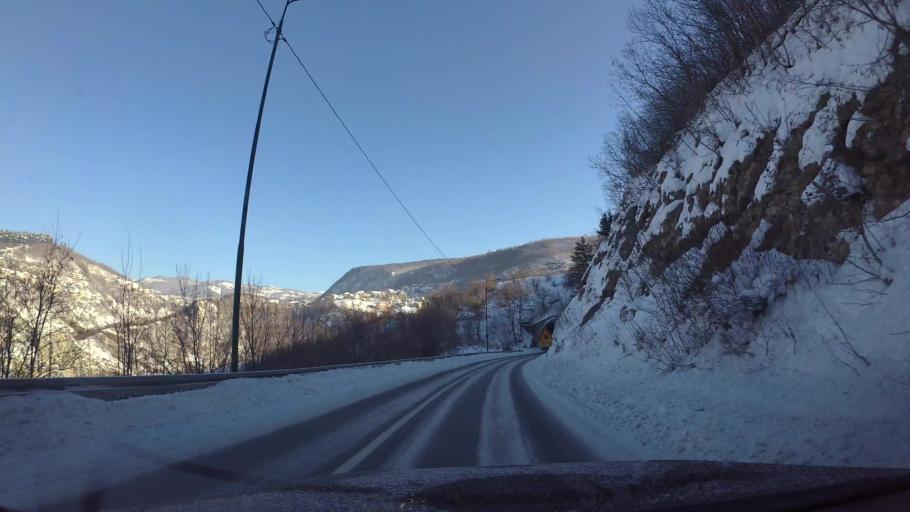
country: BA
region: Federation of Bosnia and Herzegovina
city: Kobilja Glava
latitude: 43.8569
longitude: 18.4491
